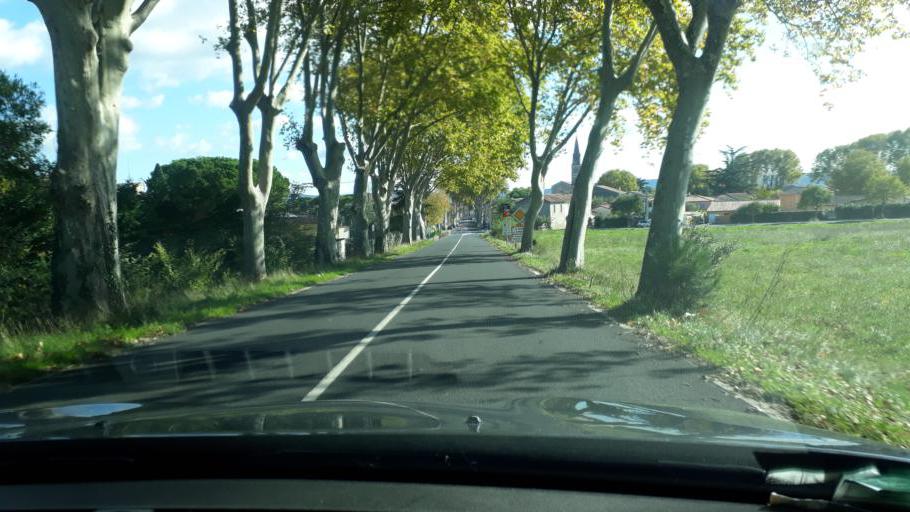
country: FR
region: Languedoc-Roussillon
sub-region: Departement de l'Herault
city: Saint-Andre-de-Sangonis
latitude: 43.6514
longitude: 3.4968
